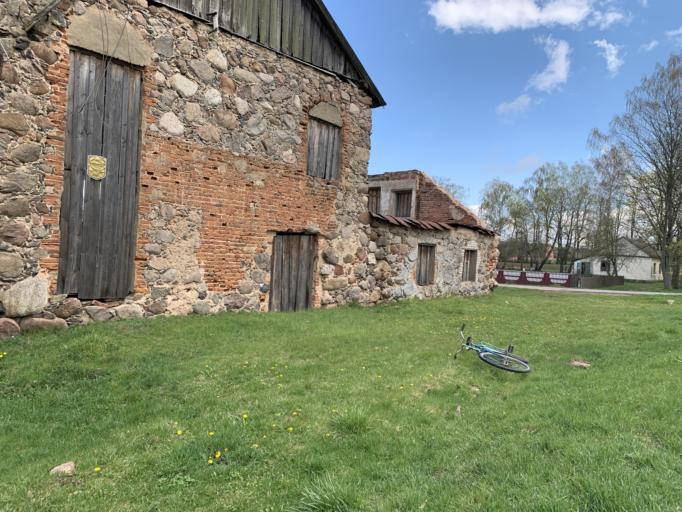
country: BY
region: Minsk
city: Kapyl'
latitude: 53.2577
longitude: 26.9545
